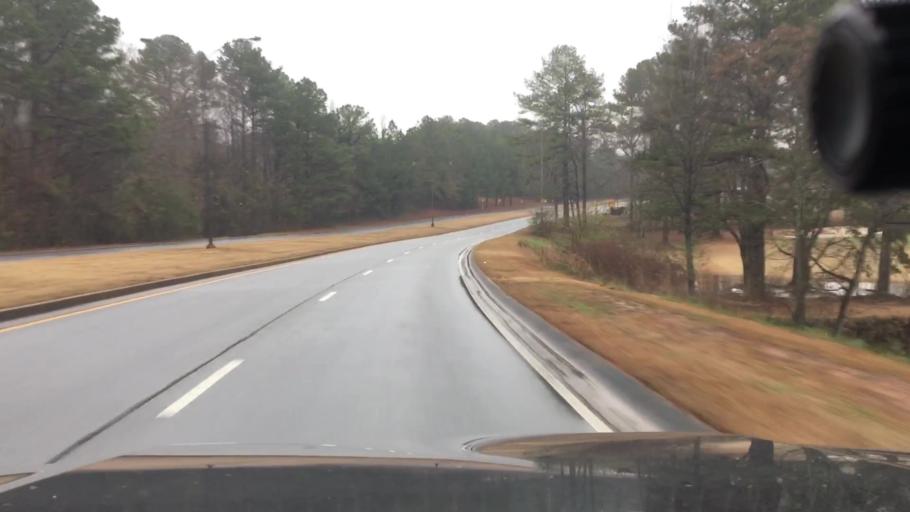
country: US
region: Georgia
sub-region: Coweta County
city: East Newnan
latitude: 33.3879
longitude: -84.7372
